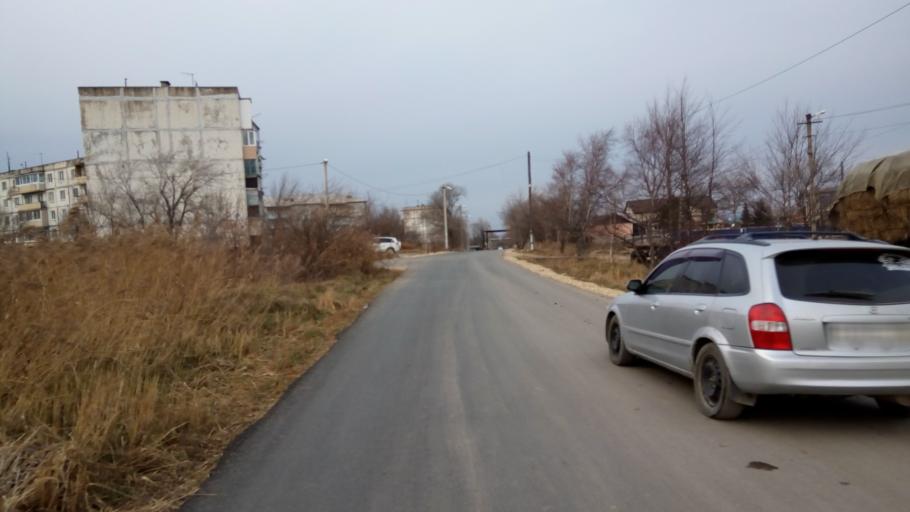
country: RU
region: Primorskiy
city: Novoshakhtinskiy
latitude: 44.0241
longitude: 132.1735
